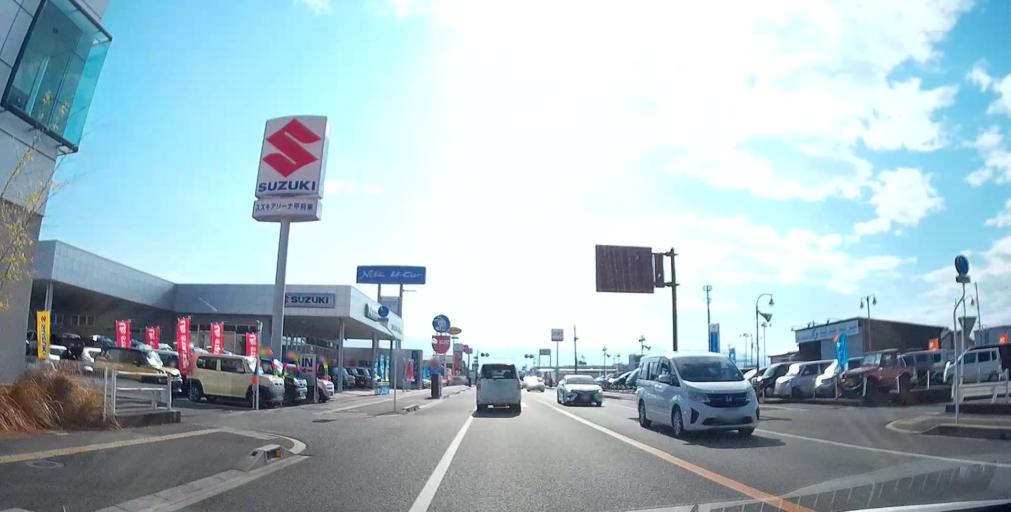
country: JP
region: Yamanashi
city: Isawa
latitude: 35.6512
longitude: 138.6133
